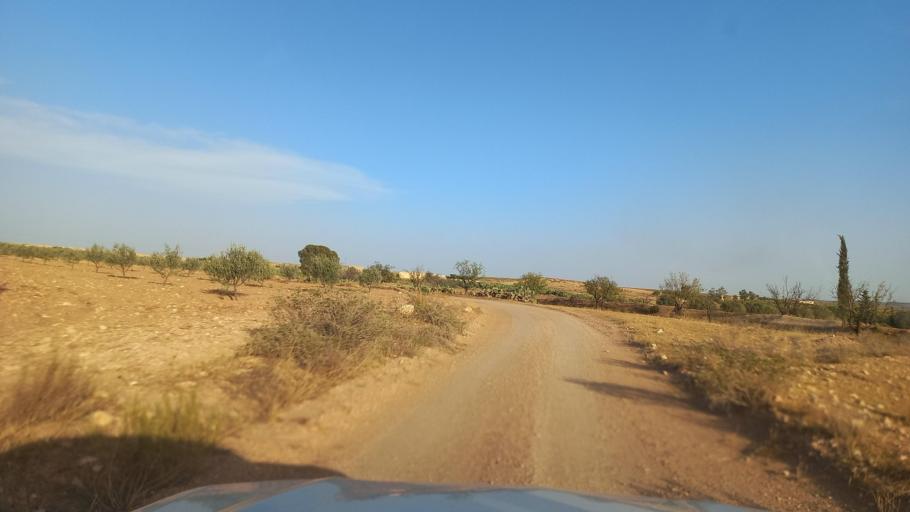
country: TN
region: Al Qasrayn
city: Kasserine
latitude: 35.2567
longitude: 8.9146
